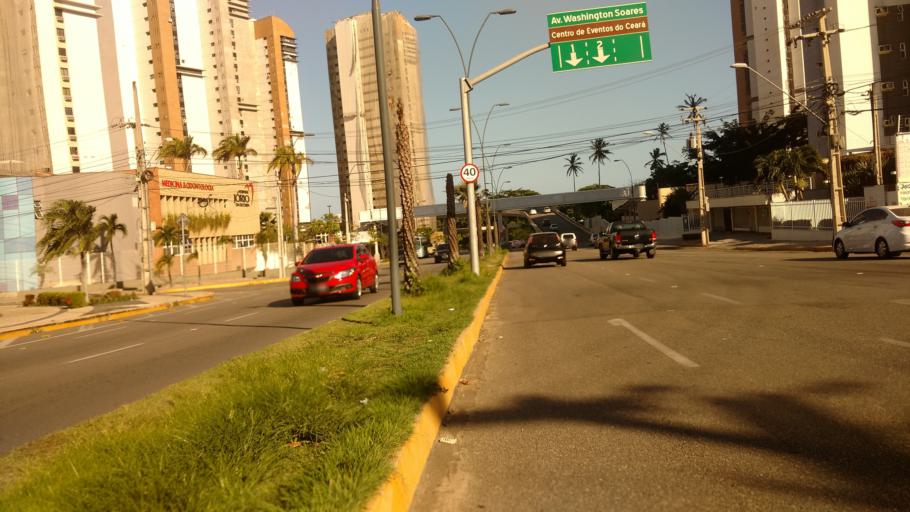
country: BR
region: Ceara
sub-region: Fortaleza
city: Fortaleza
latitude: -3.7484
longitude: -38.4926
